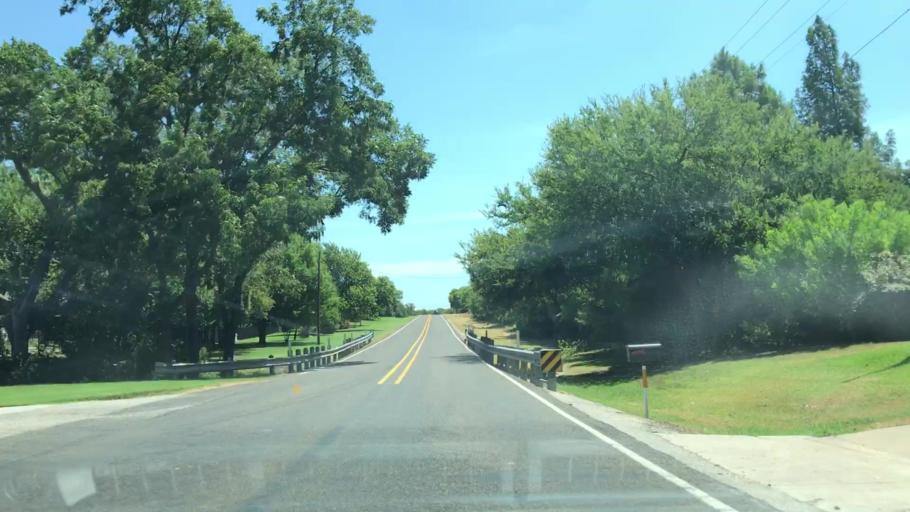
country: US
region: Texas
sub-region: Collin County
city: Fairview
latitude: 33.1562
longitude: -96.6213
